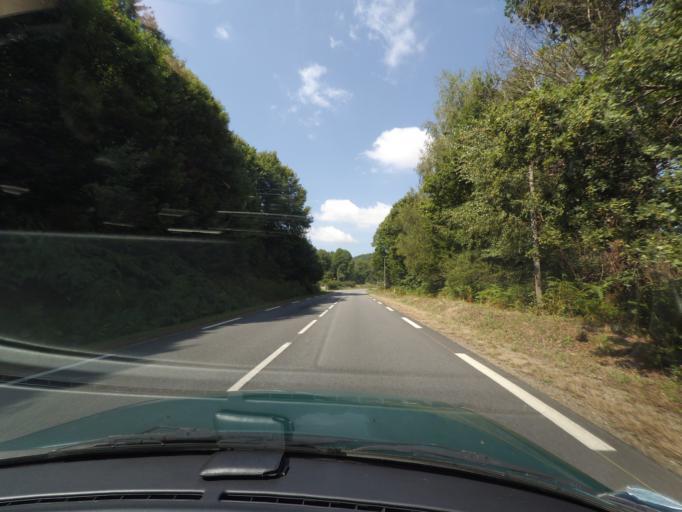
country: FR
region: Limousin
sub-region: Departement de la Haute-Vienne
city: Linards
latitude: 45.7700
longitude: 1.5284
